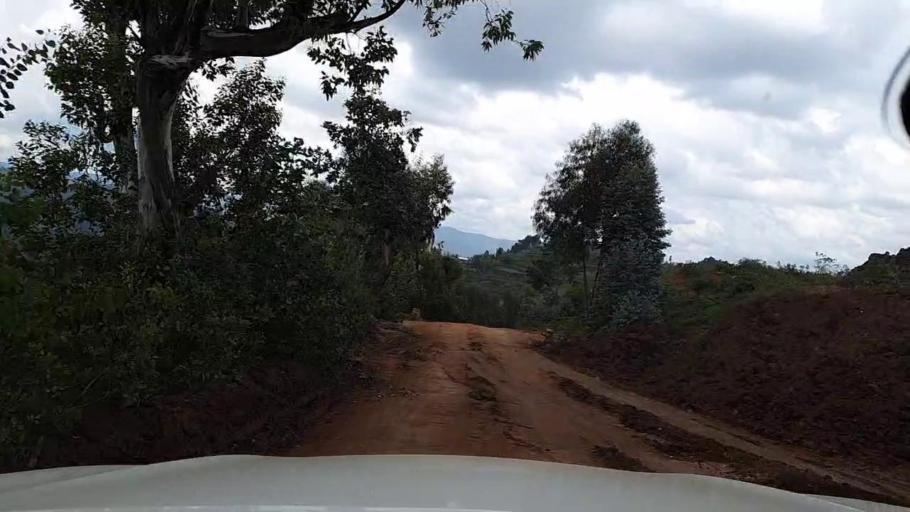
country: RW
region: Southern Province
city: Nzega
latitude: -2.7062
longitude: 29.5096
